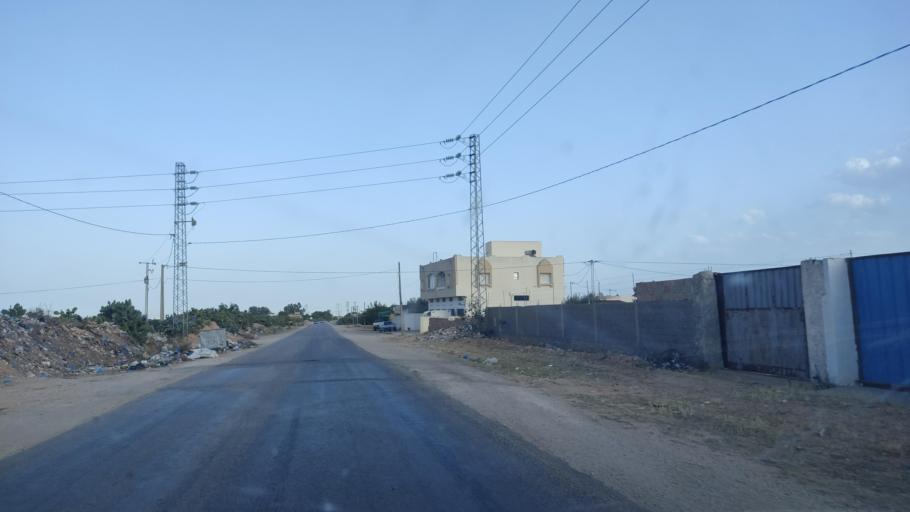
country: TN
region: Safaqis
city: Sfax
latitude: 34.8119
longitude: 10.6607
